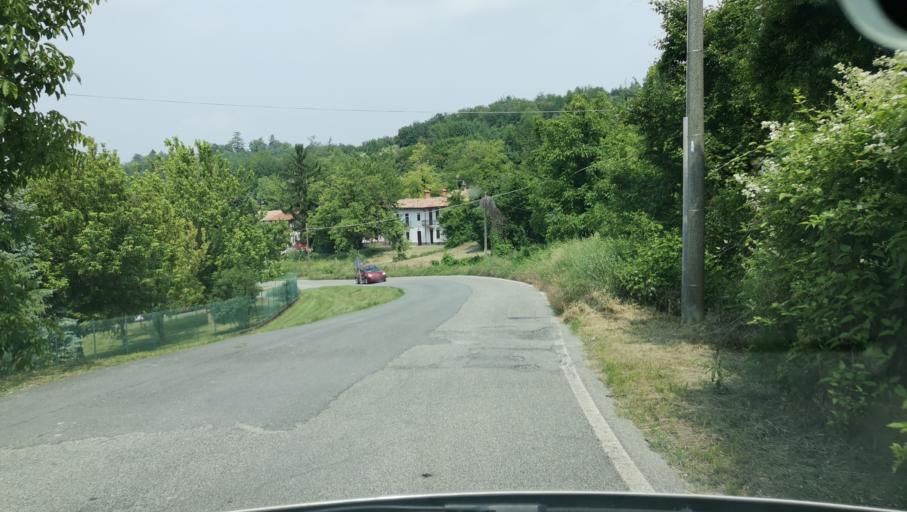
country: IT
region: Piedmont
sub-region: Provincia di Alessandria
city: Odalengo Piccolo
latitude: 45.0703
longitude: 8.2160
